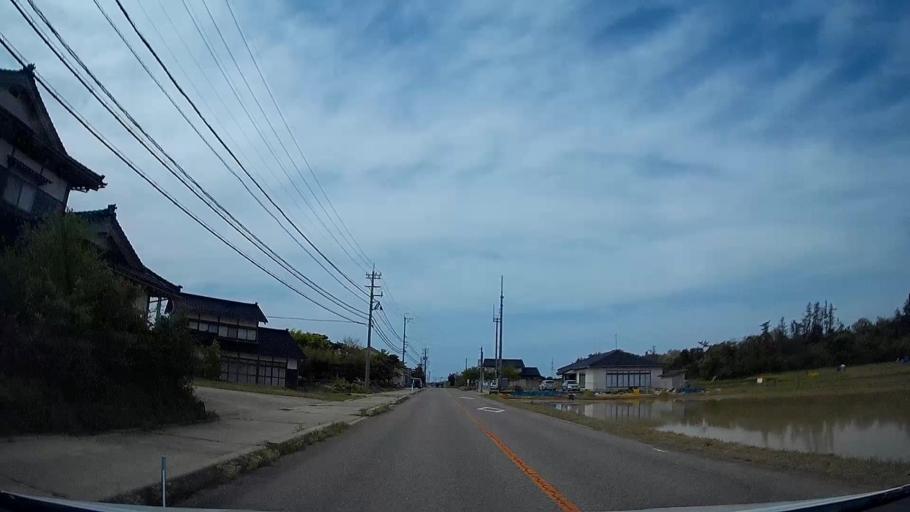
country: JP
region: Ishikawa
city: Hakui
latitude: 37.0362
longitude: 136.7454
